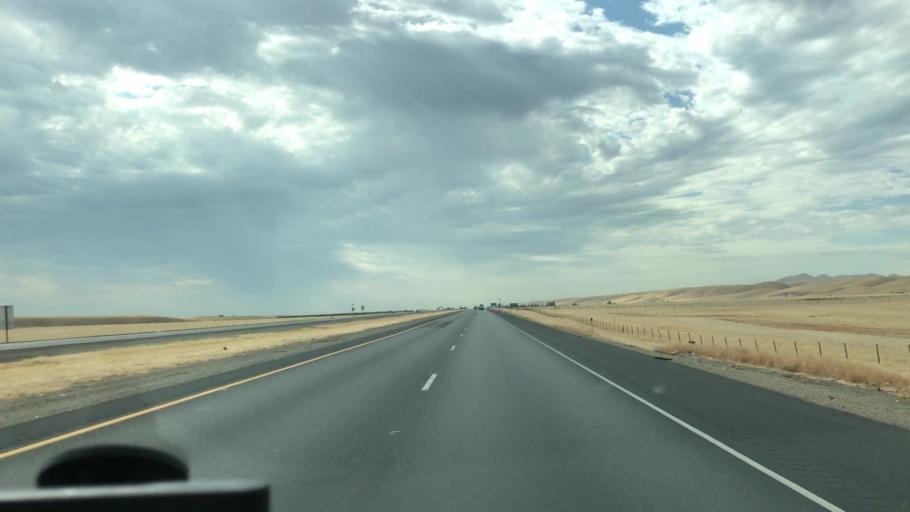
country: US
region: California
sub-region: San Joaquin County
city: Tracy
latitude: 37.6550
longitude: -121.4292
